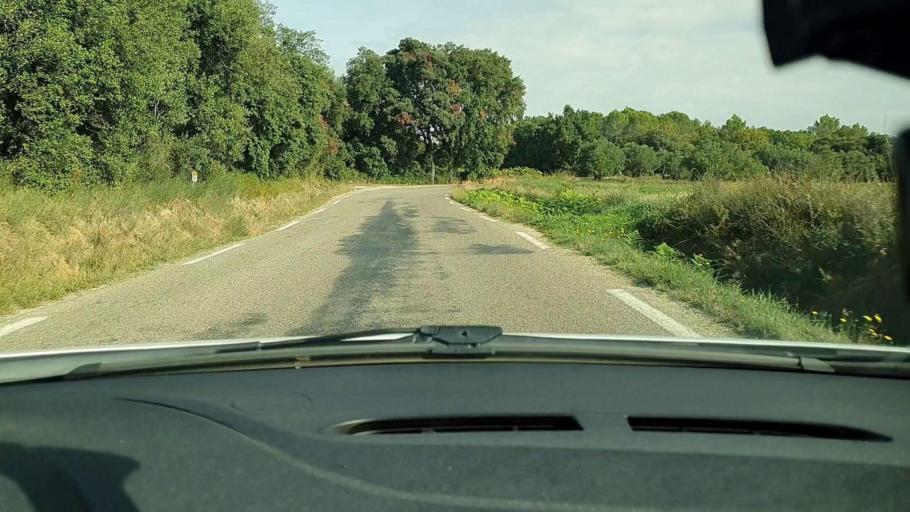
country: FR
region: Languedoc-Roussillon
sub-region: Departement du Gard
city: Saint-Quentin-la-Poterie
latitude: 44.0642
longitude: 4.4411
